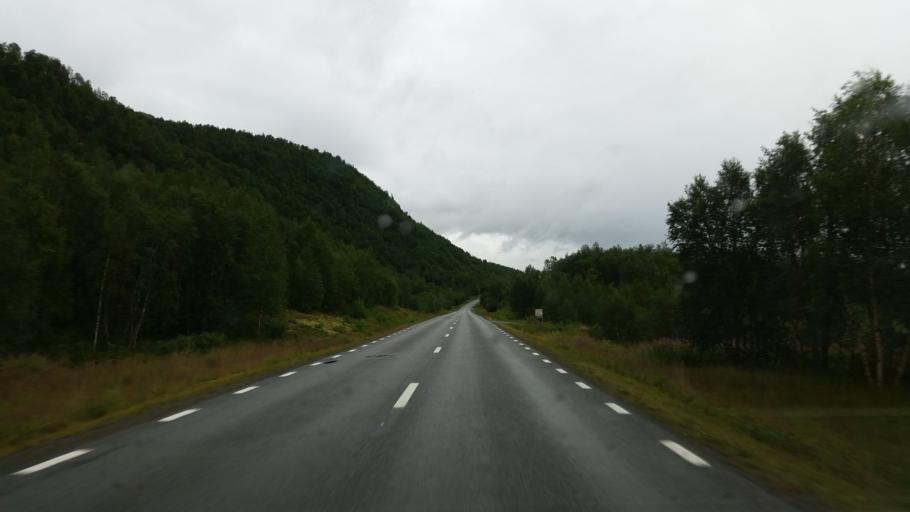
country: NO
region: Nordland
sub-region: Rana
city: Mo i Rana
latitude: 65.8783
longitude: 14.9990
